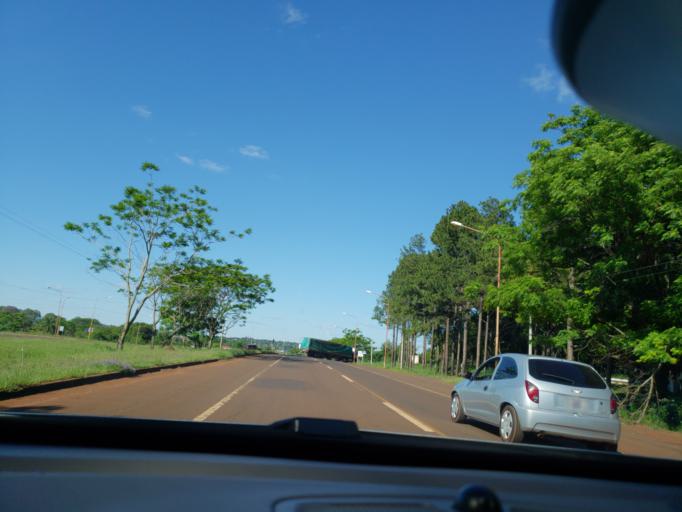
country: AR
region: Misiones
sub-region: Departamento de Capital
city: Posadas
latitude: -27.4006
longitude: -55.9650
